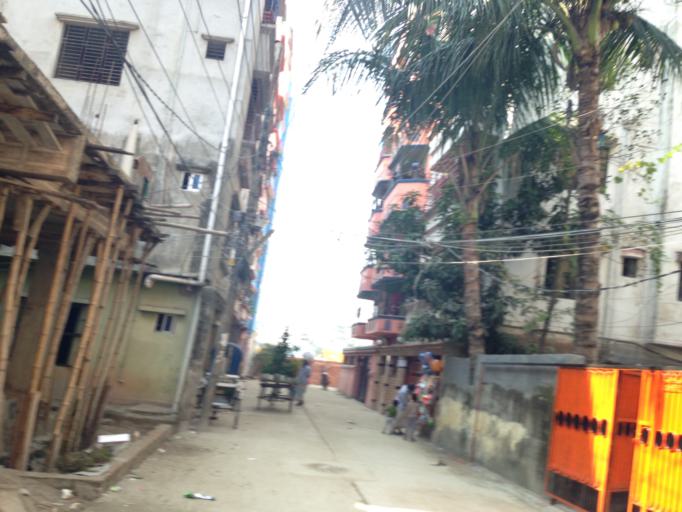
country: BD
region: Dhaka
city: Azimpur
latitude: 23.8014
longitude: 90.3458
